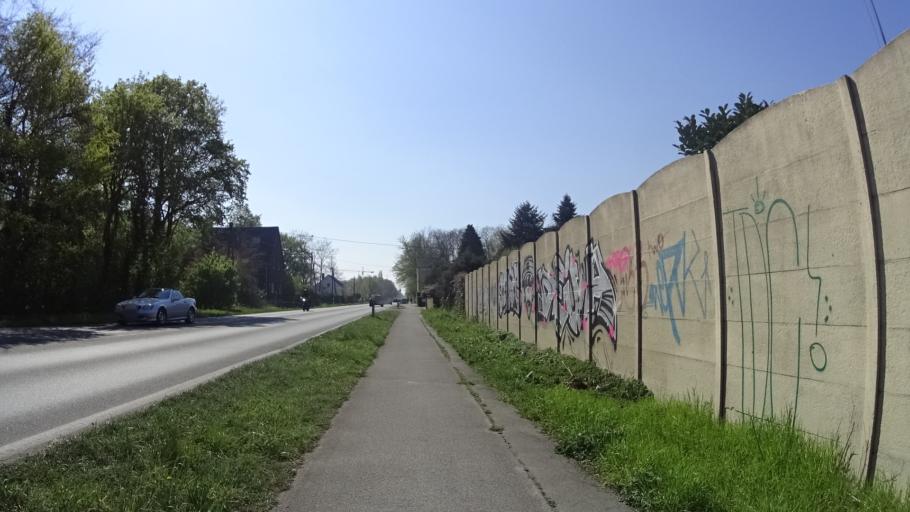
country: DE
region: North Rhine-Westphalia
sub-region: Regierungsbezirk Dusseldorf
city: Moers
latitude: 51.4779
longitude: 6.6322
